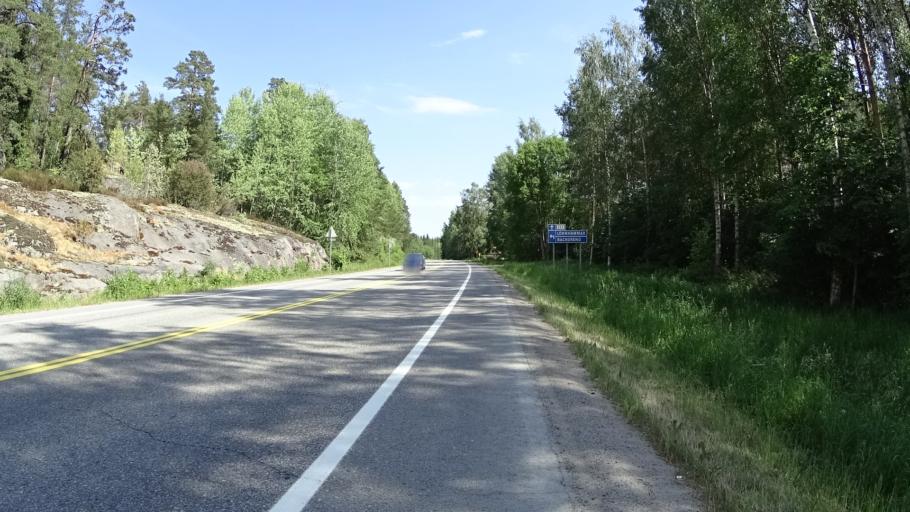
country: FI
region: Uusimaa
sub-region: Raaseporin
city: Karis
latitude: 60.0884
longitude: 23.6477
